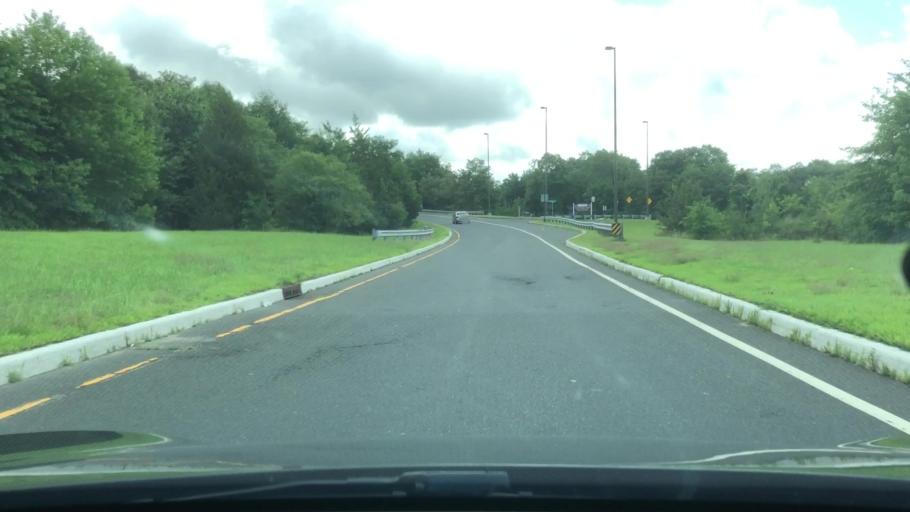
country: US
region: New Jersey
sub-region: Monmouth County
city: West Freehold
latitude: 40.2534
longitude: -74.3332
